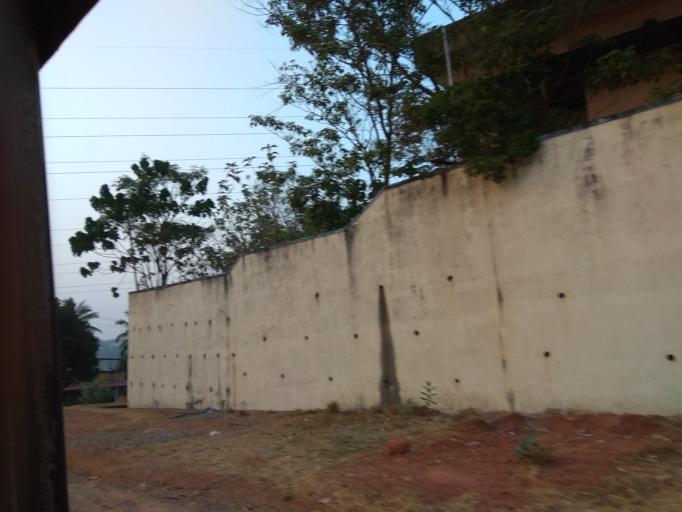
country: IN
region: Karnataka
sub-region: Dakshina Kannada
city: Mangalore
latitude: 12.9284
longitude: 74.8669
